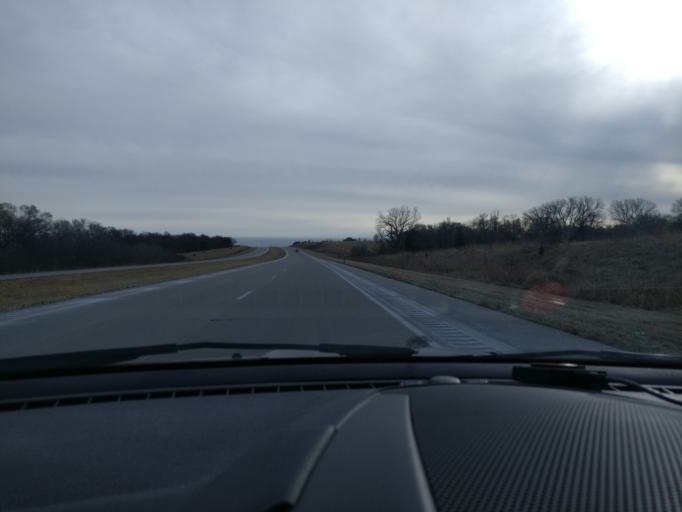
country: US
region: Nebraska
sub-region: Saunders County
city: Wahoo
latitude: 41.1838
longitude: -96.6337
